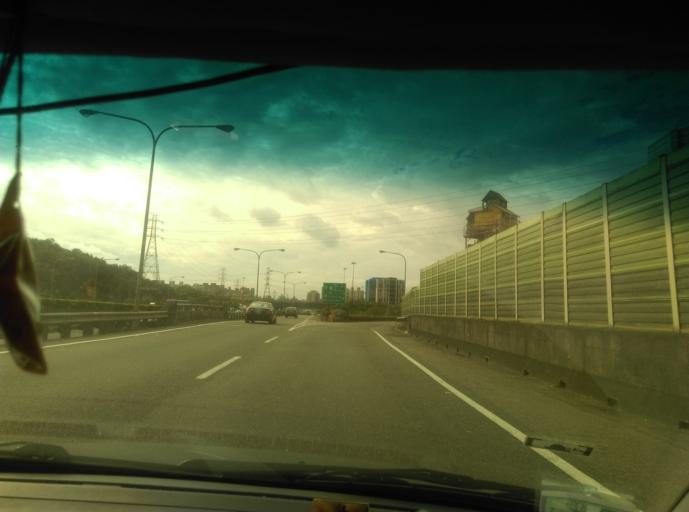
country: TW
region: Taiwan
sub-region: Keelung
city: Keelung
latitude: 25.0736
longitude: 121.6513
